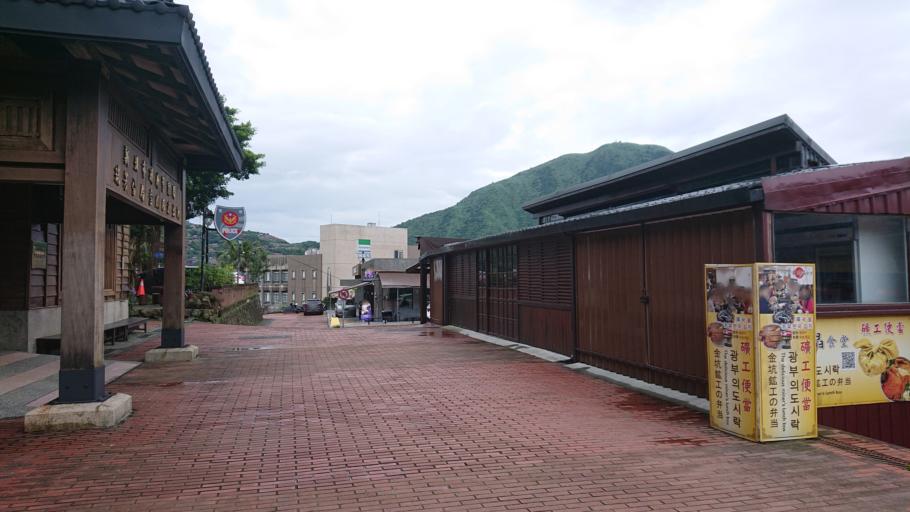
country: TW
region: Taiwan
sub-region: Keelung
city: Keelung
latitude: 25.1083
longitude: 121.8579
